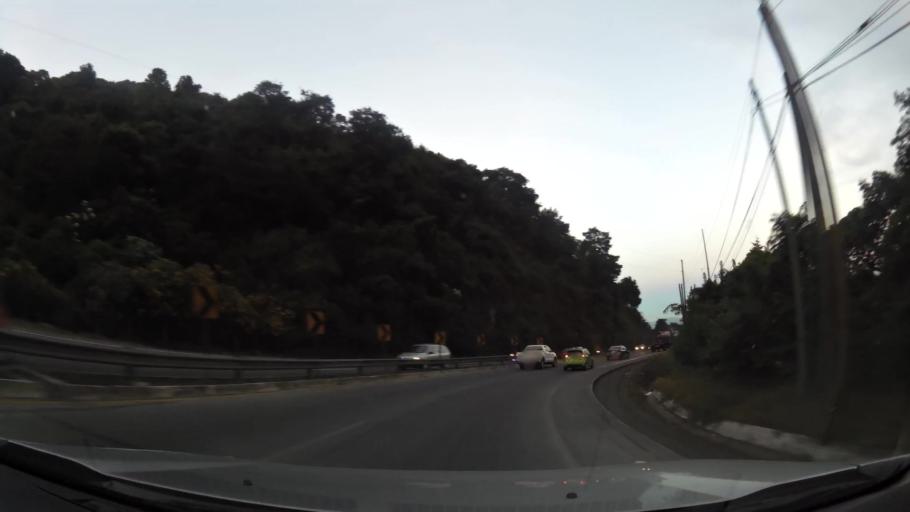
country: GT
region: Guatemala
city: Mixco
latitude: 14.6101
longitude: -90.6254
